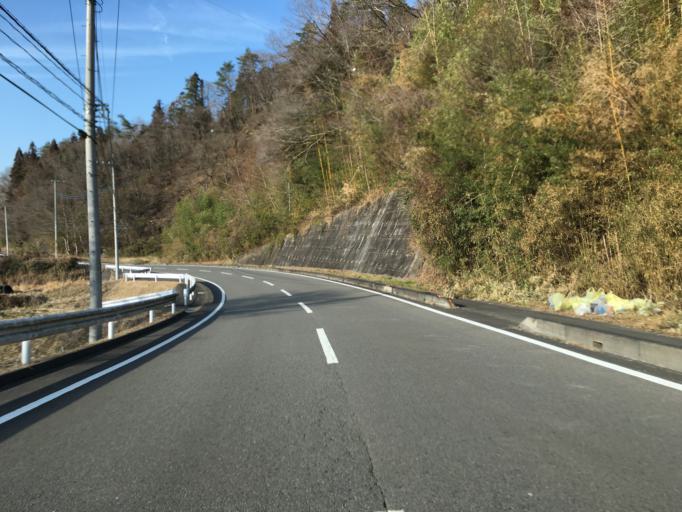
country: JP
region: Ibaraki
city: Daigo
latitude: 36.7608
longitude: 140.4353
